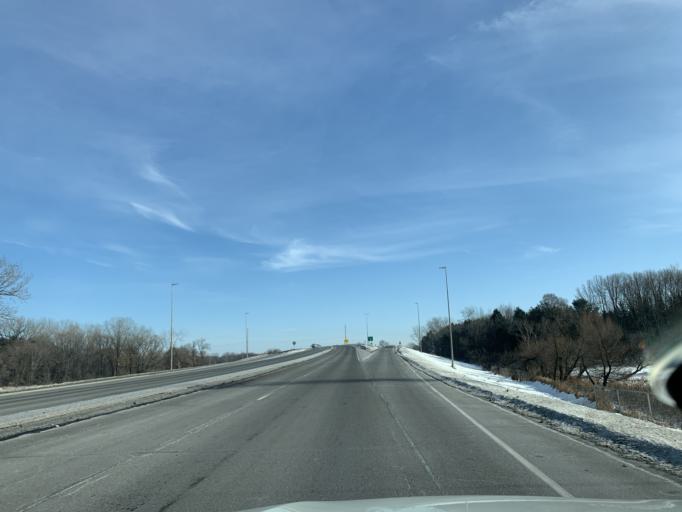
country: US
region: Minnesota
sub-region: Washington County
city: Forest Lake
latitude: 45.2892
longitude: -92.9911
